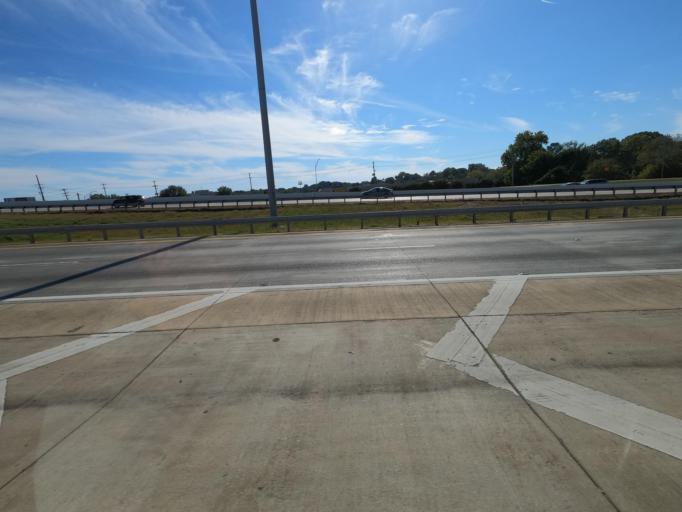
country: US
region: Tennessee
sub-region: Shelby County
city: Bartlett
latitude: 35.1549
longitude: -89.8892
